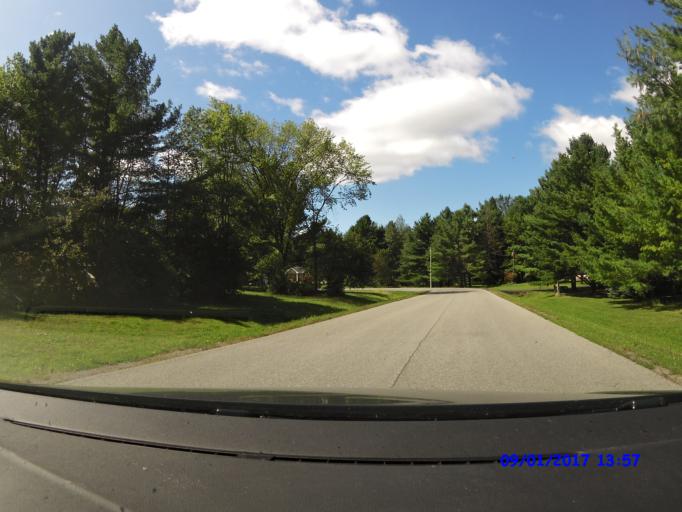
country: CA
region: Ontario
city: Bells Corners
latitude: 45.3554
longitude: -75.9630
